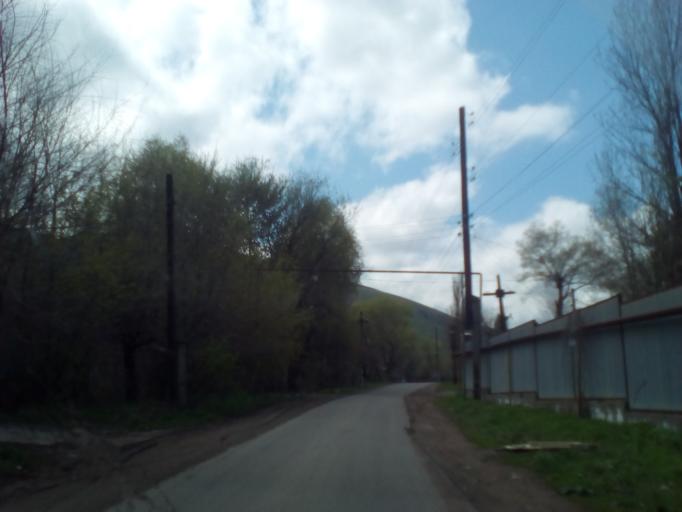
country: KZ
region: Almaty Oblysy
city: Burunday
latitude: 43.1554
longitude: 76.4323
